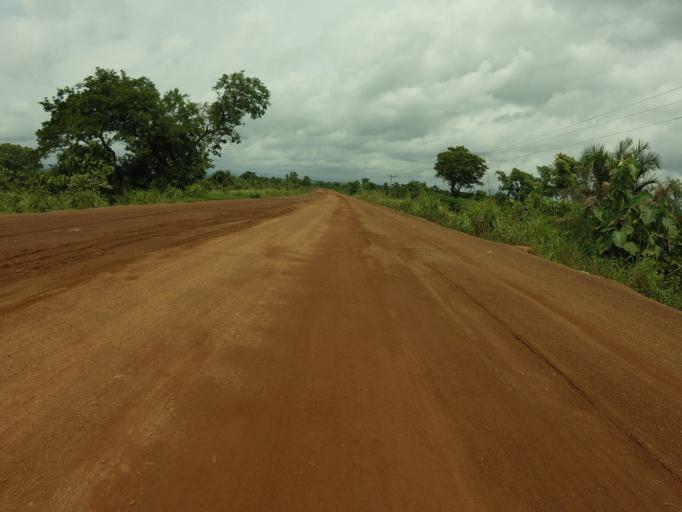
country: GH
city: Kpandae
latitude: 8.4073
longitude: 0.3969
